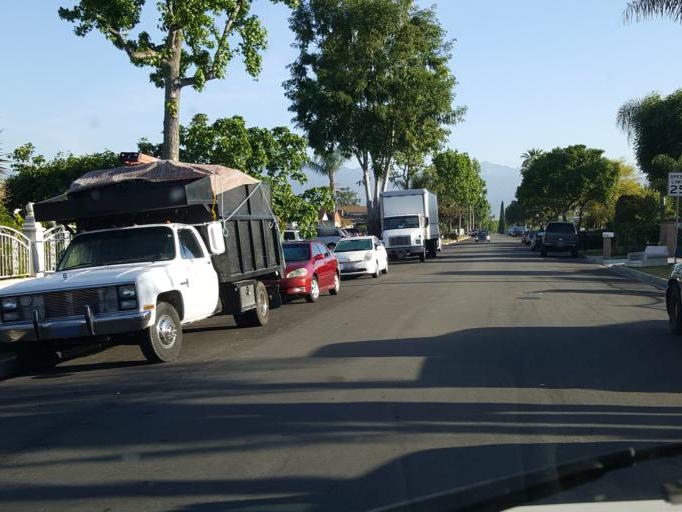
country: US
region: California
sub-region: Los Angeles County
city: Valinda
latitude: 34.0442
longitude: -117.9243
